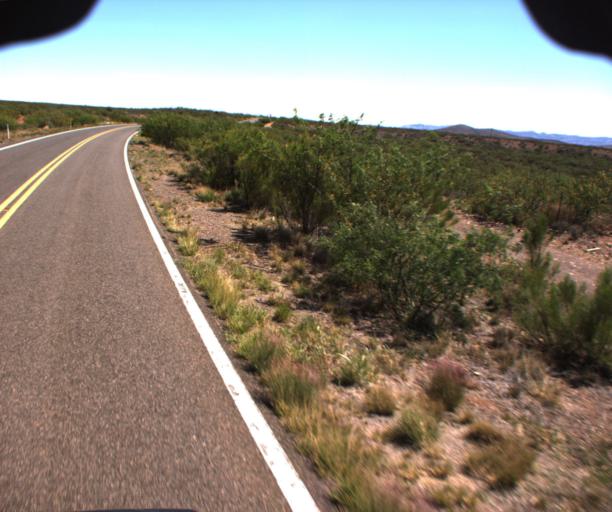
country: US
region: Arizona
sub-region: Cochise County
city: Douglas
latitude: 31.4937
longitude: -109.3374
